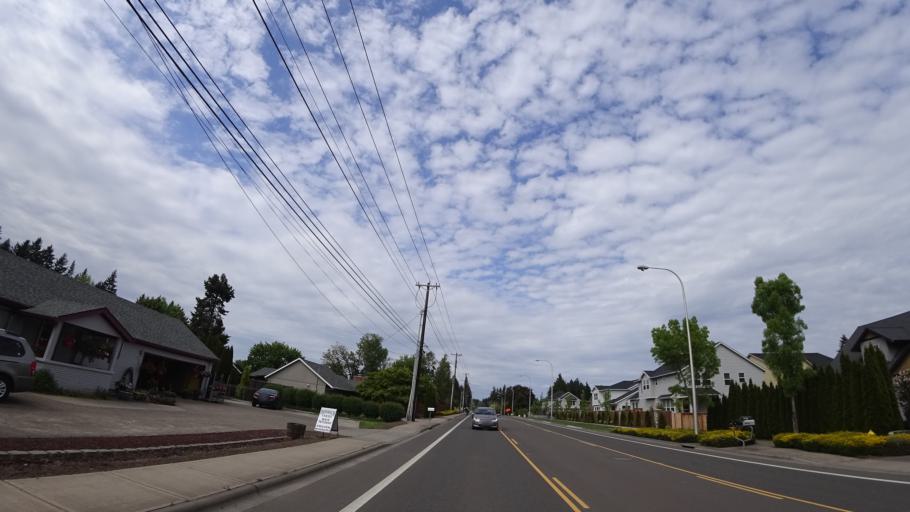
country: US
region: Oregon
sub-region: Washington County
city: Hillsboro
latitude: 45.5142
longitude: -122.9367
